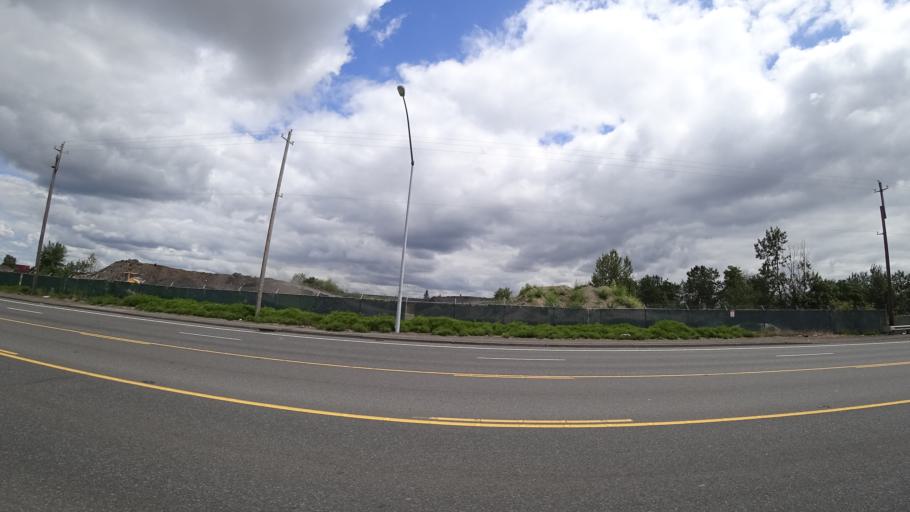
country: US
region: Oregon
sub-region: Multnomah County
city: Portland
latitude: 45.5660
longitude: -122.5979
